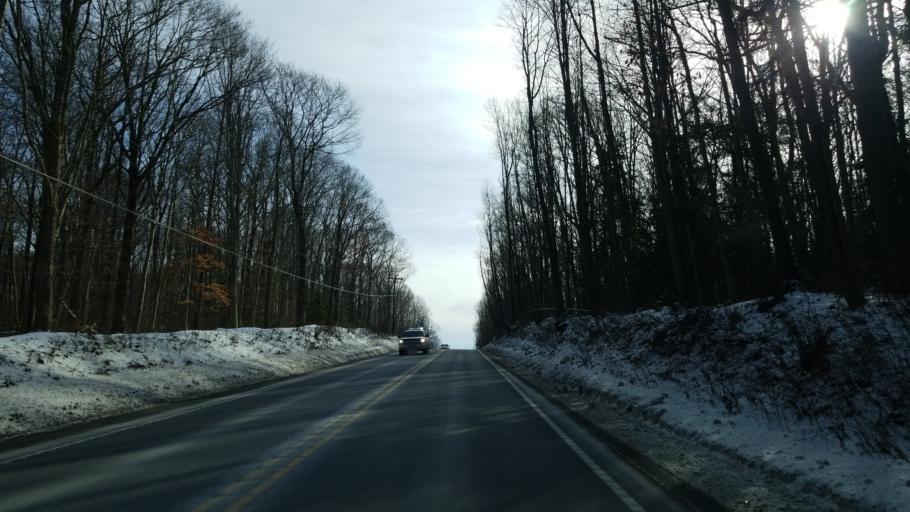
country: US
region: Pennsylvania
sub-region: Clearfield County
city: Clearfield
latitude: 41.1326
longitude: -78.5384
